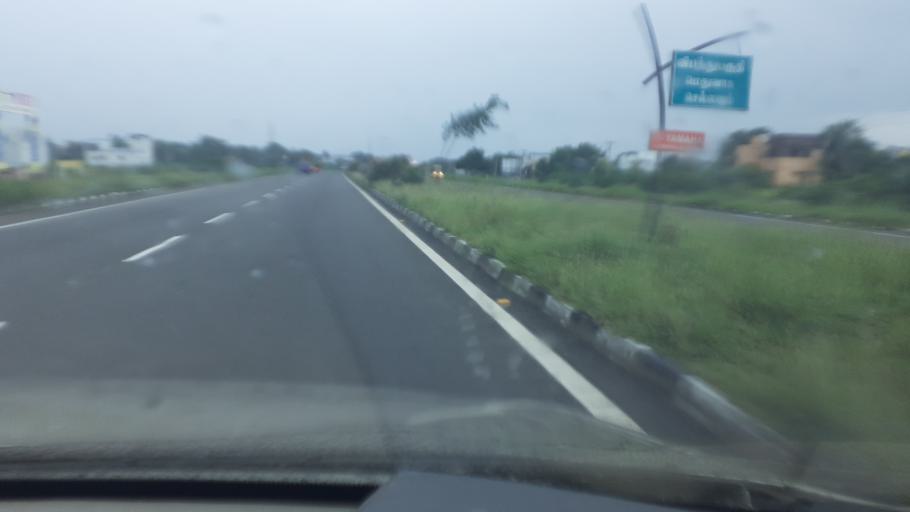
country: IN
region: Tamil Nadu
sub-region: Virudhunagar
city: Virudunagar
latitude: 9.6203
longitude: 77.9577
